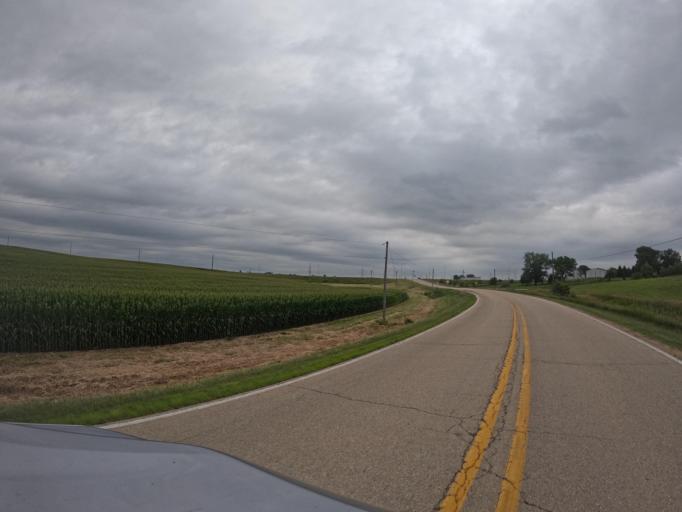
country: US
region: Iowa
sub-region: Clinton County
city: De Witt
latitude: 41.8695
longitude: -90.5749
